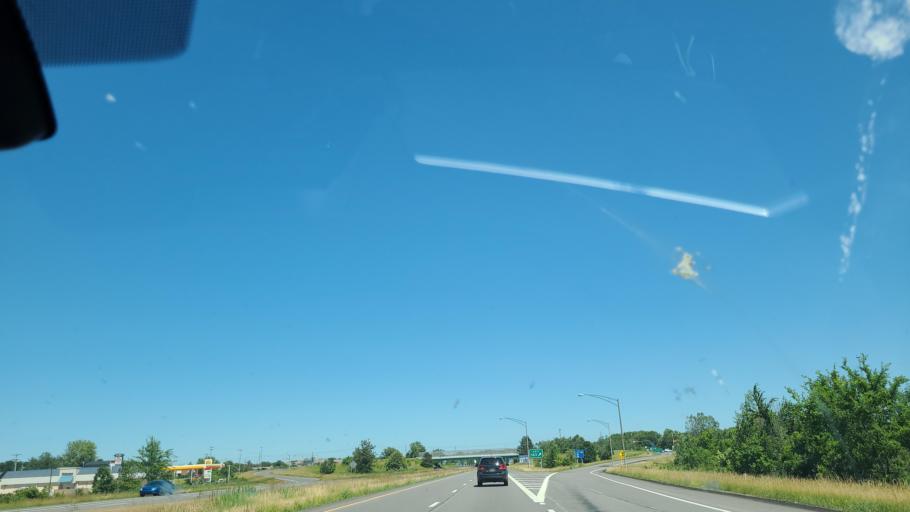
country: US
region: Ohio
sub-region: Lorain County
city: Amherst
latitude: 41.4108
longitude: -82.2441
